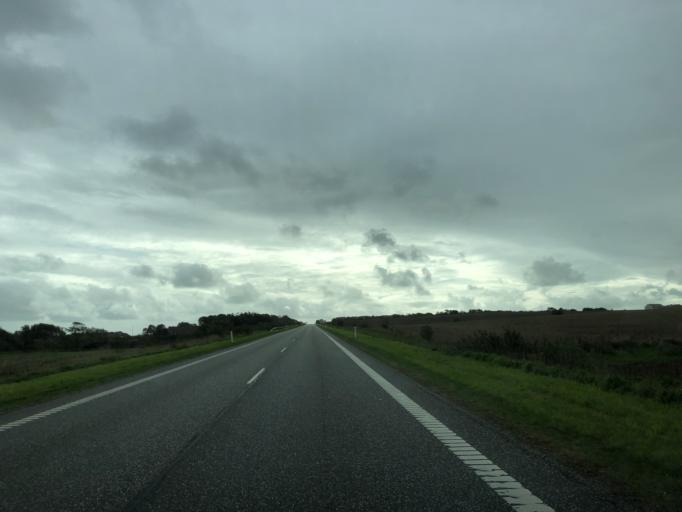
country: DK
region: North Denmark
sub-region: Thisted Kommune
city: Hurup
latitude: 56.7631
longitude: 8.4547
